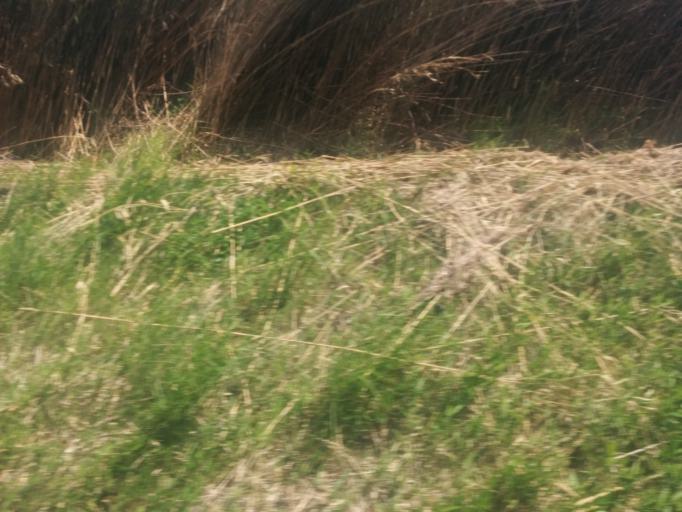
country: JP
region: Osaka
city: Kashihara
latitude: 34.5520
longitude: 135.6741
